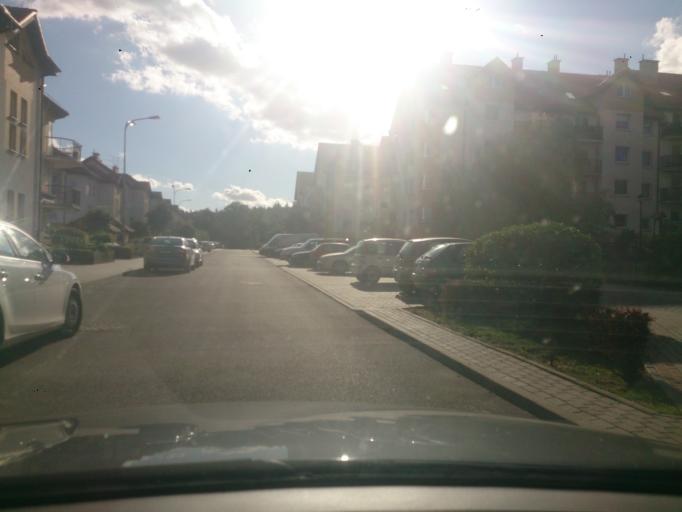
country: PL
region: Pomeranian Voivodeship
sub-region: Gdynia
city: Wielki Kack
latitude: 54.4654
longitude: 18.4872
